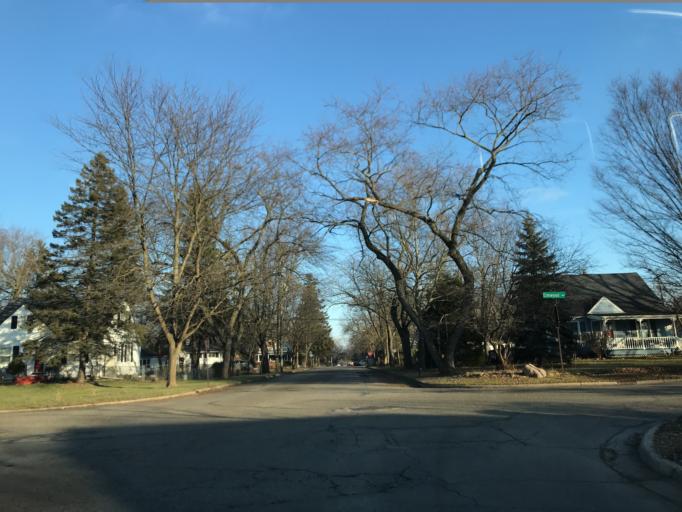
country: US
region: Michigan
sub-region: Washtenaw County
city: Ann Arbor
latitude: 42.2472
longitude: -83.6992
